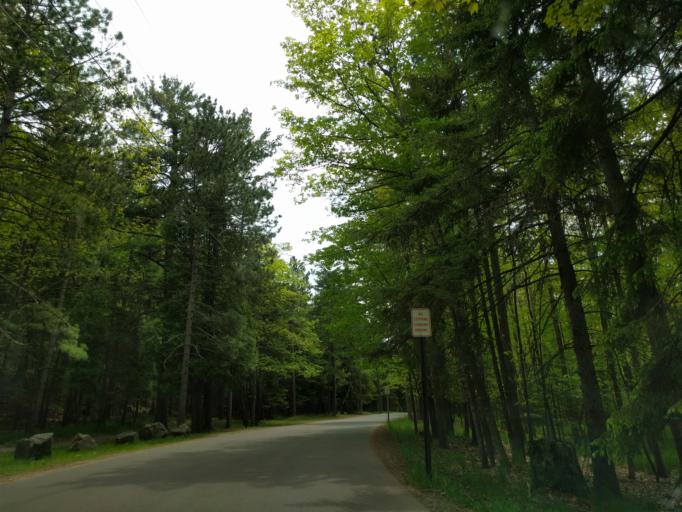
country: US
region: Michigan
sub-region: Marquette County
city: Marquette
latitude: 46.5849
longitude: -87.3841
